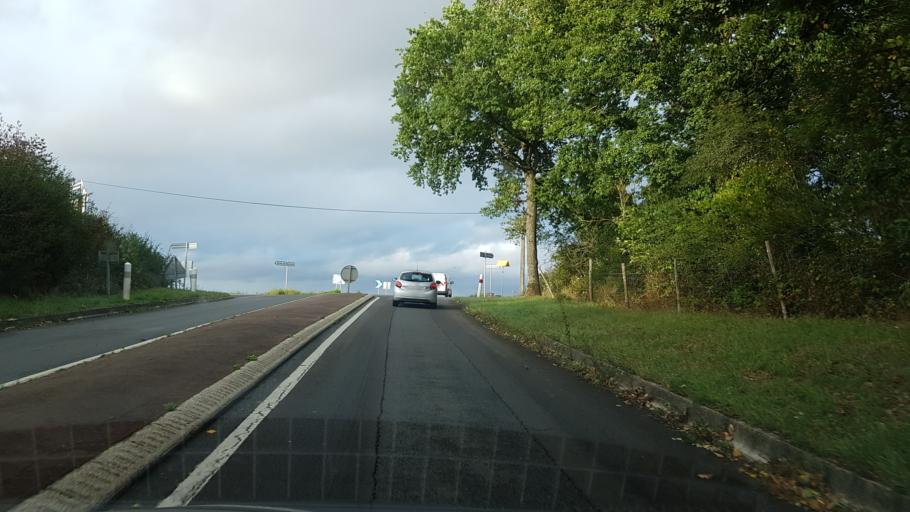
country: FR
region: Ile-de-France
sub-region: Departement de l'Essonne
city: Fontenay-les-Briis
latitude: 48.6319
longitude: 2.1767
